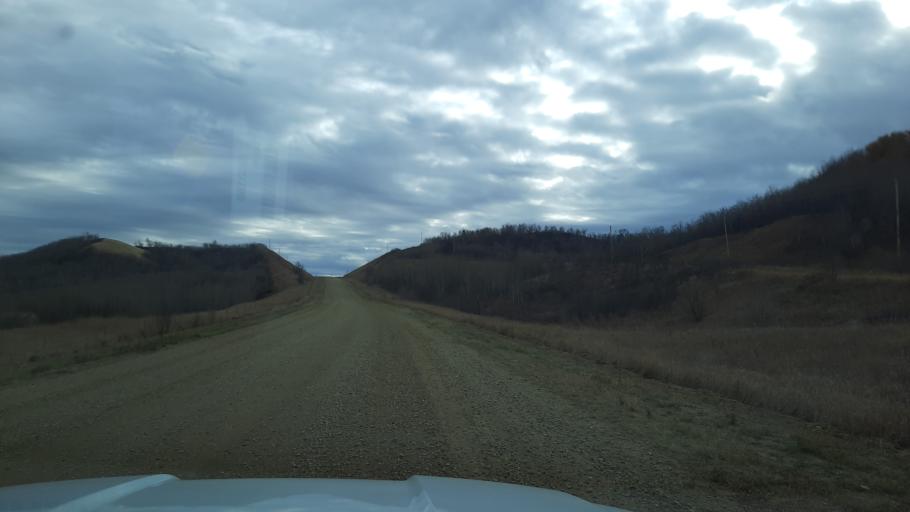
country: CA
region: Saskatchewan
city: Pilot Butte
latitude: 50.7702
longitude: -104.2804
